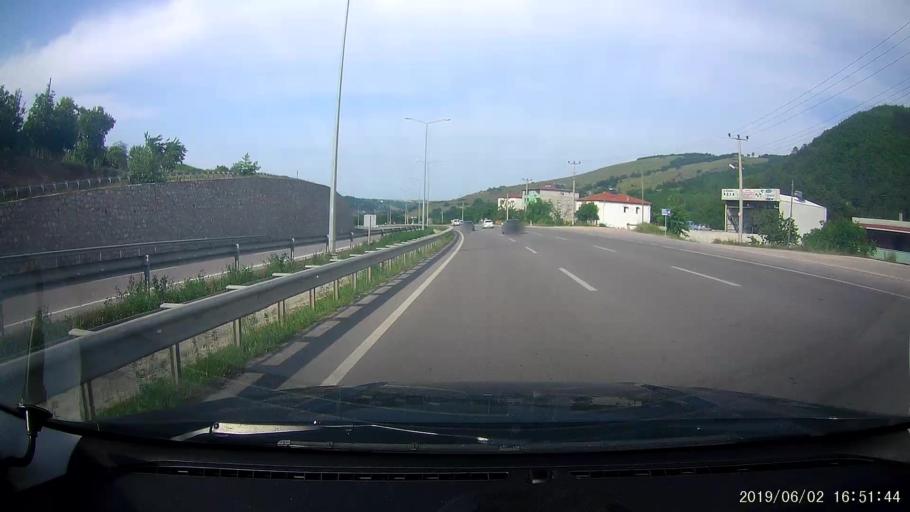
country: TR
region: Samsun
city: Samsun
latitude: 41.2776
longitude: 36.1873
